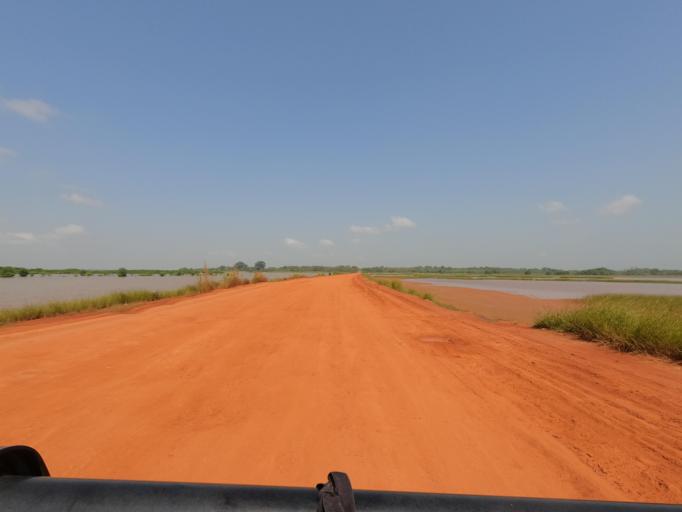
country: GW
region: Cacheu
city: Canchungo
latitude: 12.2578
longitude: -15.7812
